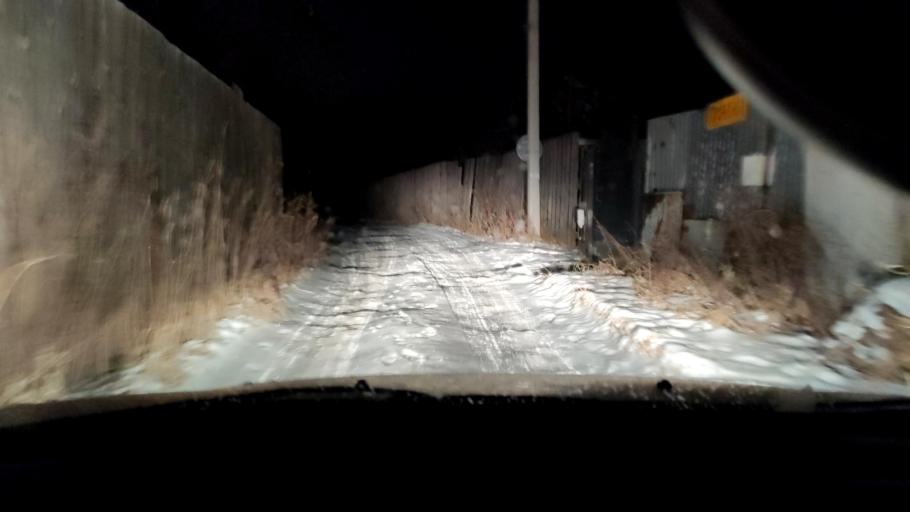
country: RU
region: Perm
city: Froly
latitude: 57.9455
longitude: 56.1884
